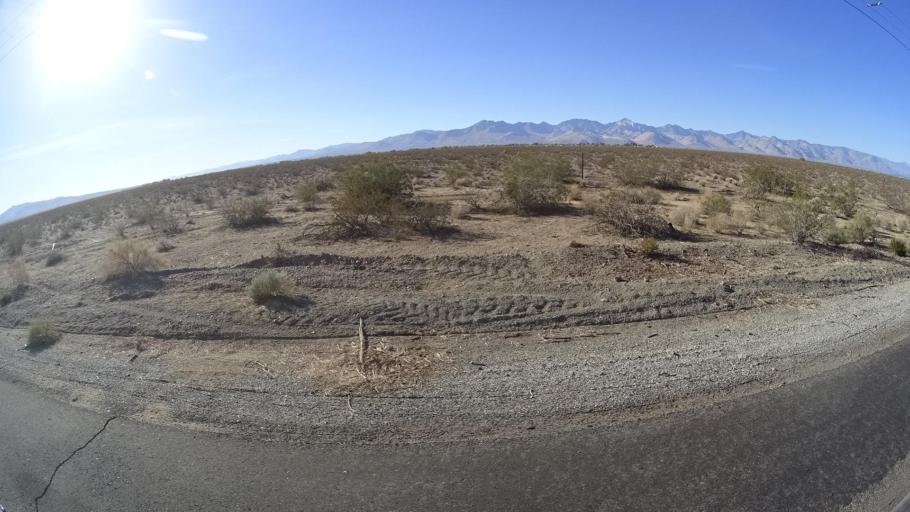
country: US
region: California
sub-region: Kern County
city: China Lake Acres
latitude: 35.6414
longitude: -117.7231
